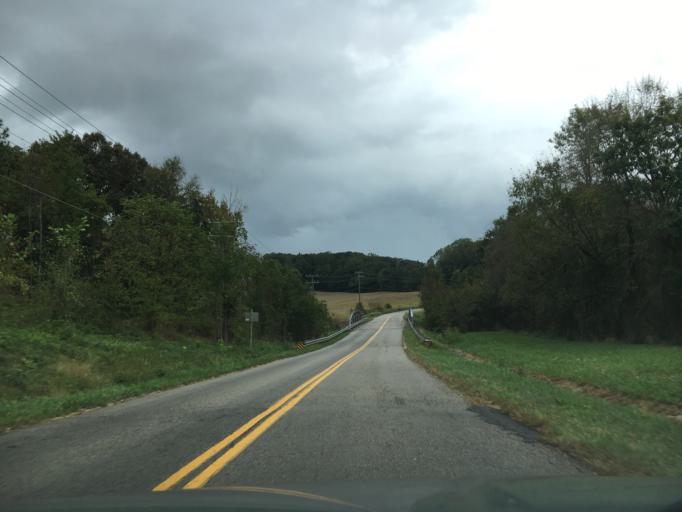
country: US
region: Virginia
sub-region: Amelia County
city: Amelia Court House
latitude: 37.3843
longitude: -77.9791
